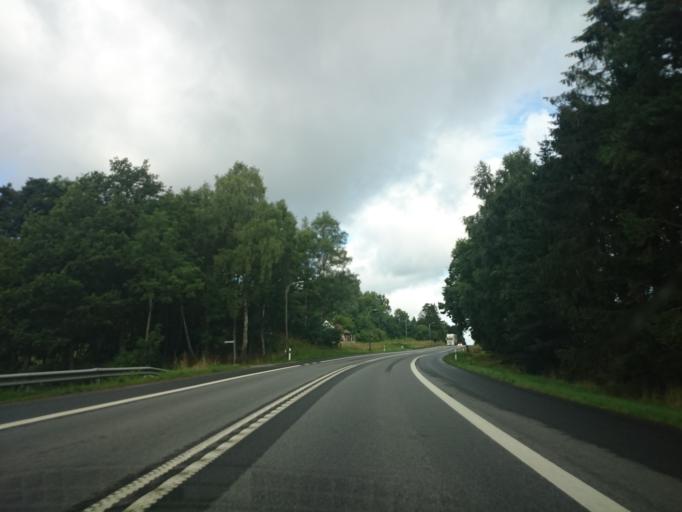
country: SE
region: Skane
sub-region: Kristianstads Kommun
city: Onnestad
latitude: 55.9295
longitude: 13.9303
